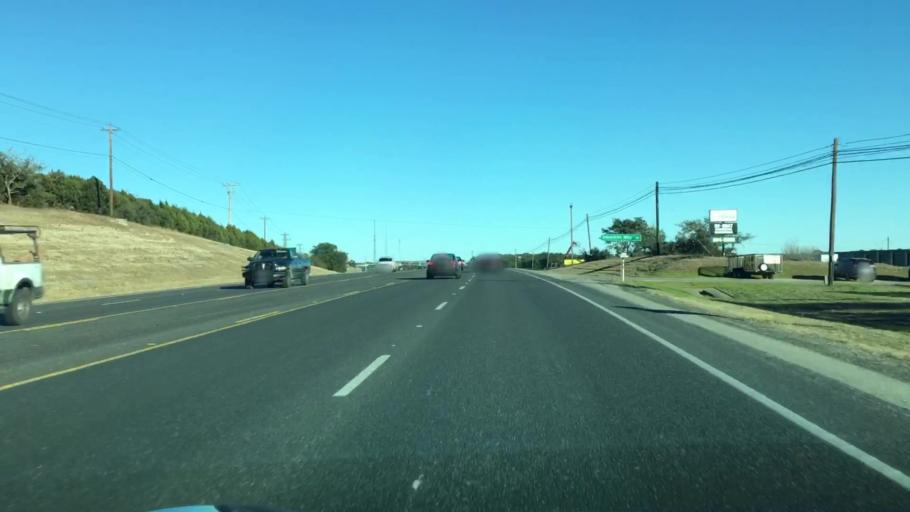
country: US
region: Texas
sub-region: Hays County
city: Dripping Springs
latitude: 30.1941
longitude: -98.0342
